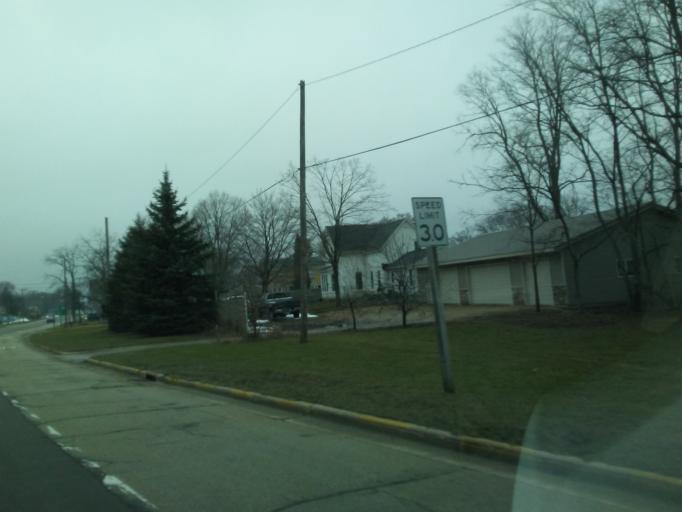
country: US
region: Wisconsin
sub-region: Dane County
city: Mazomanie
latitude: 43.1720
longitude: -89.7920
